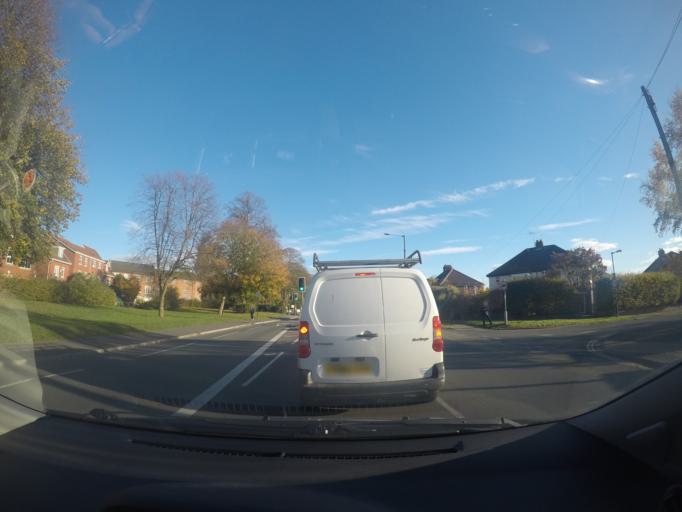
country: GB
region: England
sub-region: City of York
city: Nether Poppleton
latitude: 53.9654
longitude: -1.1238
